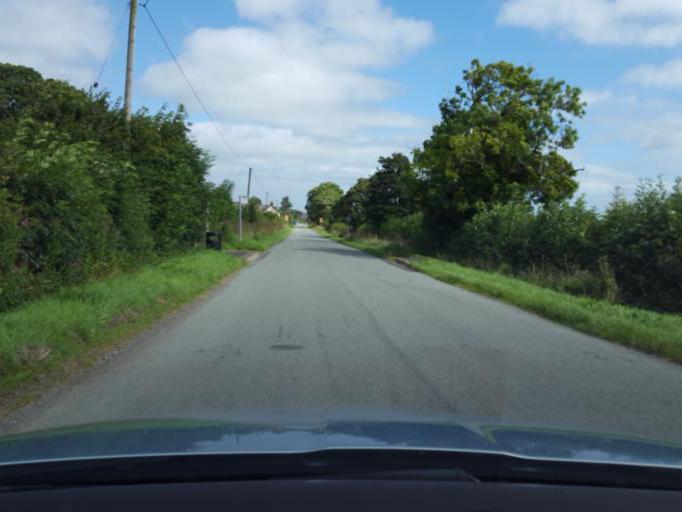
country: GB
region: Wales
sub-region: County of Flintshire
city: Leeswood
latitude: 53.1096
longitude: -3.1306
